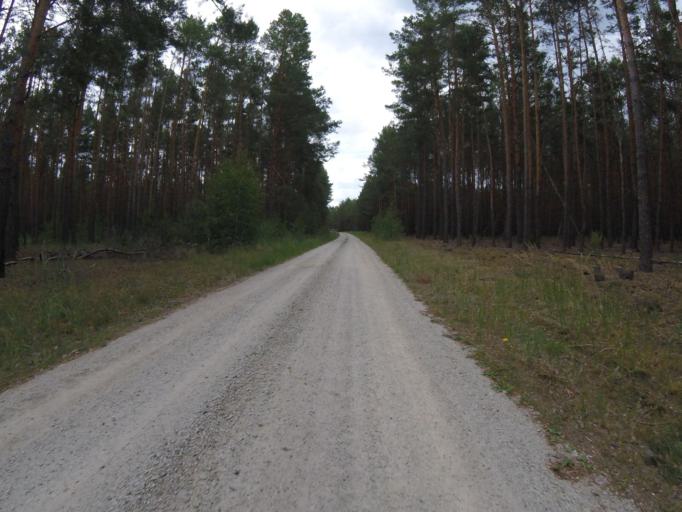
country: DE
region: Brandenburg
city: Halbe
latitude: 52.1313
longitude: 13.7280
